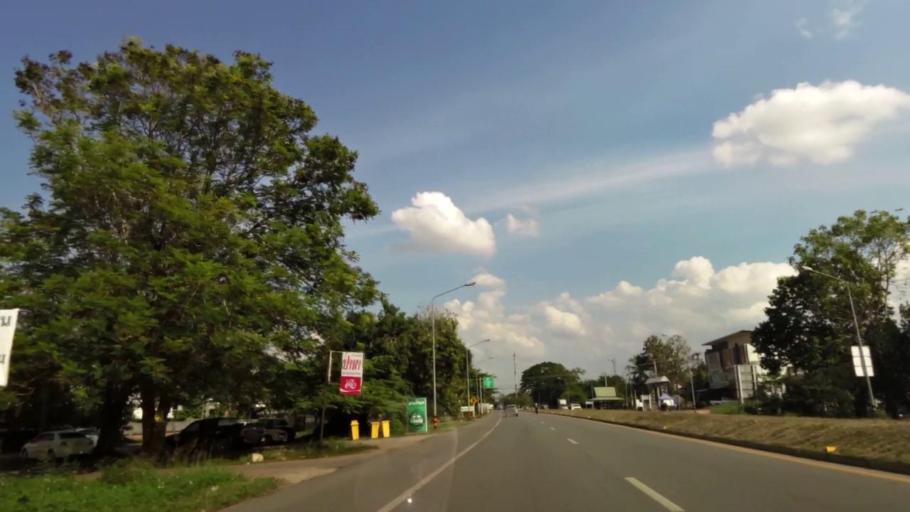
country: TH
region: Phrae
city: Phrae
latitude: 18.1346
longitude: 100.1288
